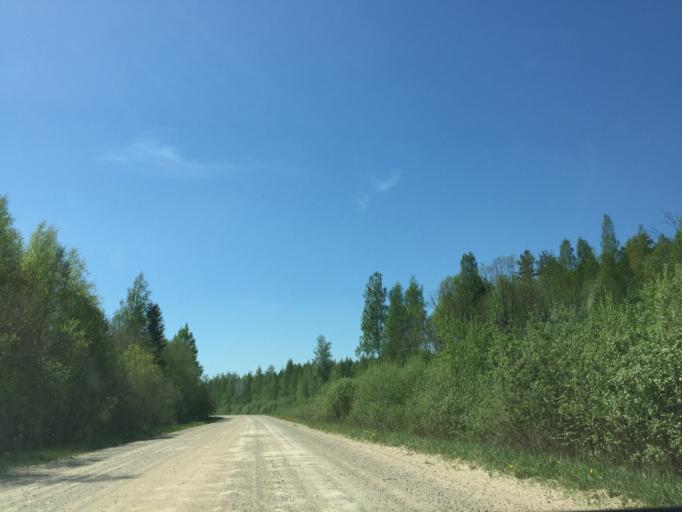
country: LV
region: Kegums
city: Kegums
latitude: 56.8791
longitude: 24.7815
